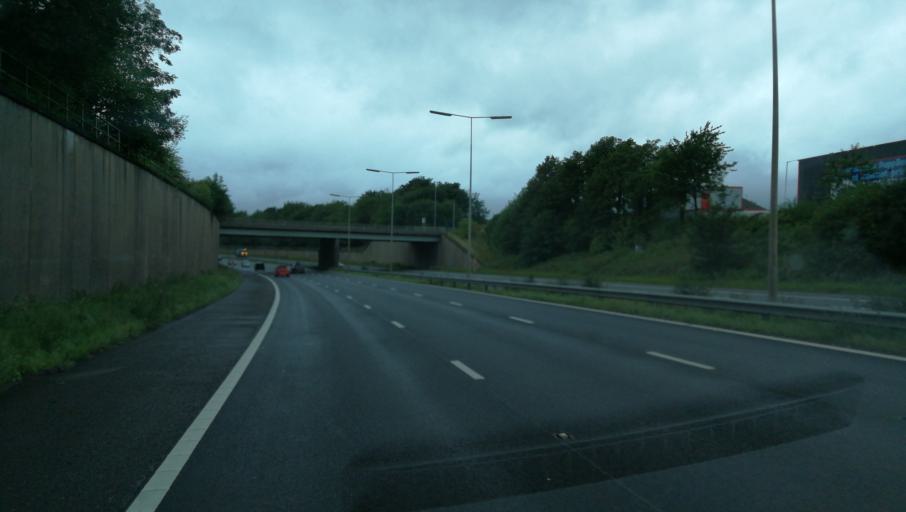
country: GB
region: England
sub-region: Borough of Bolton
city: Farnworth
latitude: 53.5383
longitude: -2.3981
